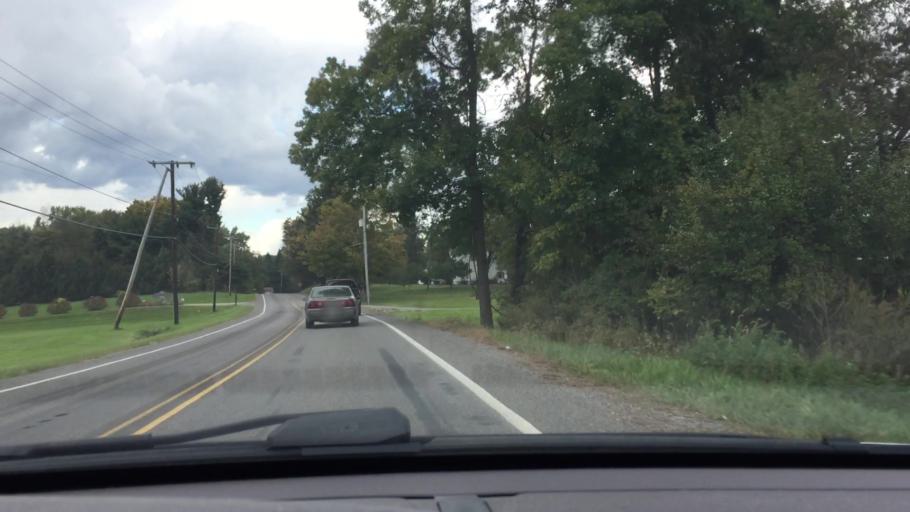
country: US
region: Pennsylvania
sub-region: Lawrence County
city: Oakwood
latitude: 41.0013
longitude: -80.4375
